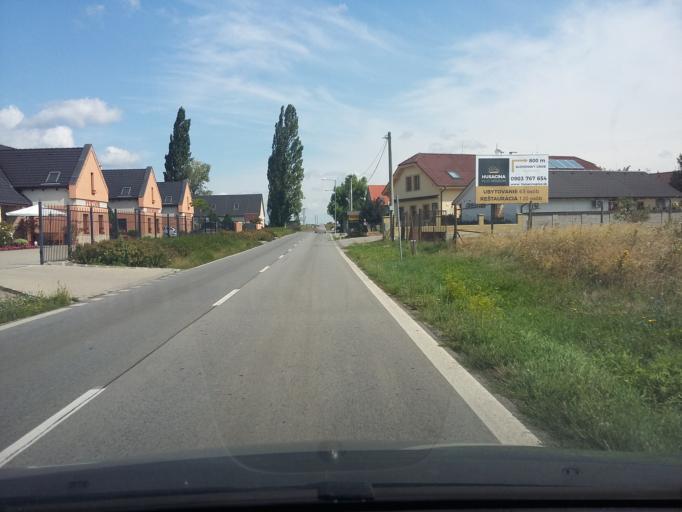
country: SK
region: Bratislavsky
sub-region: Okres Pezinok
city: Pezinok
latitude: 48.2555
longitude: 17.2624
